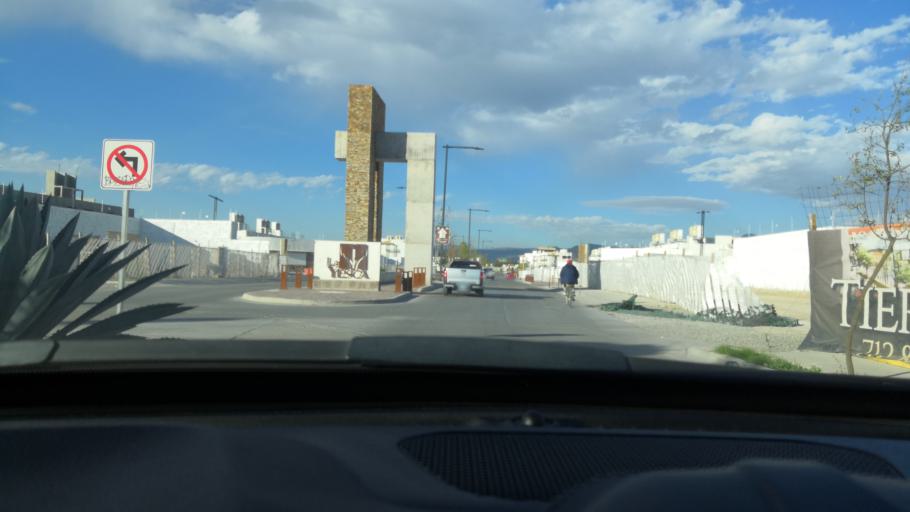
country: MX
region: Guanajuato
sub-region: Leon
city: San Jose de Duran (Los Troncoso)
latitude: 21.0833
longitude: -101.6540
